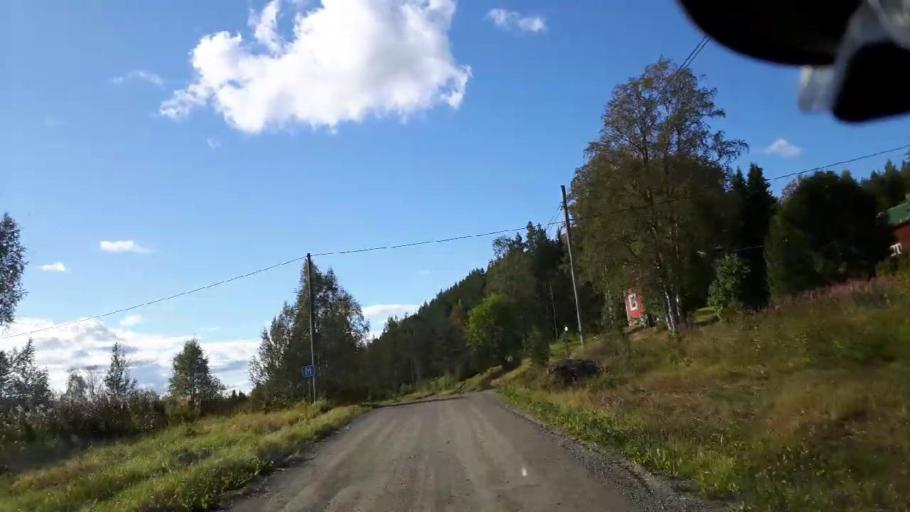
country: SE
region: Jaemtland
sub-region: Ragunda Kommun
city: Hammarstrand
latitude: 63.4751
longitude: 16.1668
